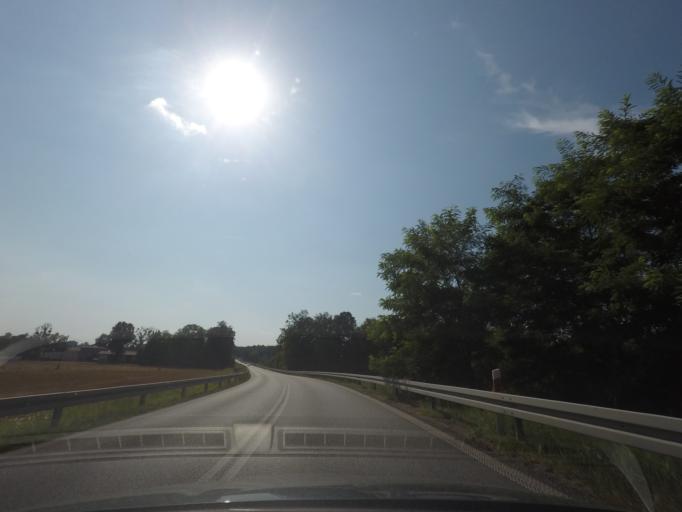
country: PL
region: Silesian Voivodeship
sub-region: Powiat pszczynski
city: Kryry
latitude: 50.0272
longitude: 18.8265
